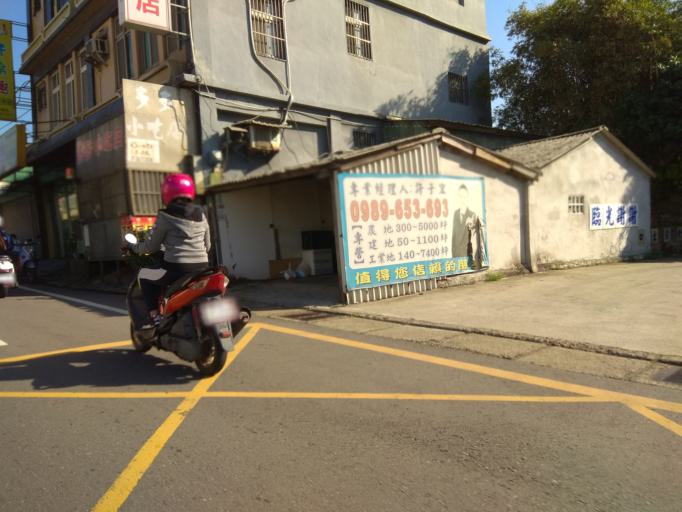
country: TW
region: Taiwan
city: Taoyuan City
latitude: 25.0658
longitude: 121.1854
